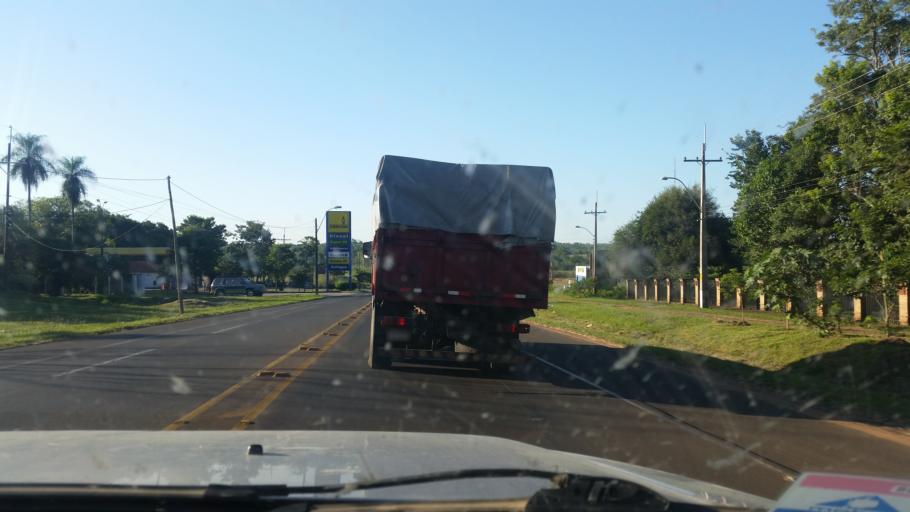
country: PY
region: Misiones
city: Santa Maria
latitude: -26.8750
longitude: -57.0323
